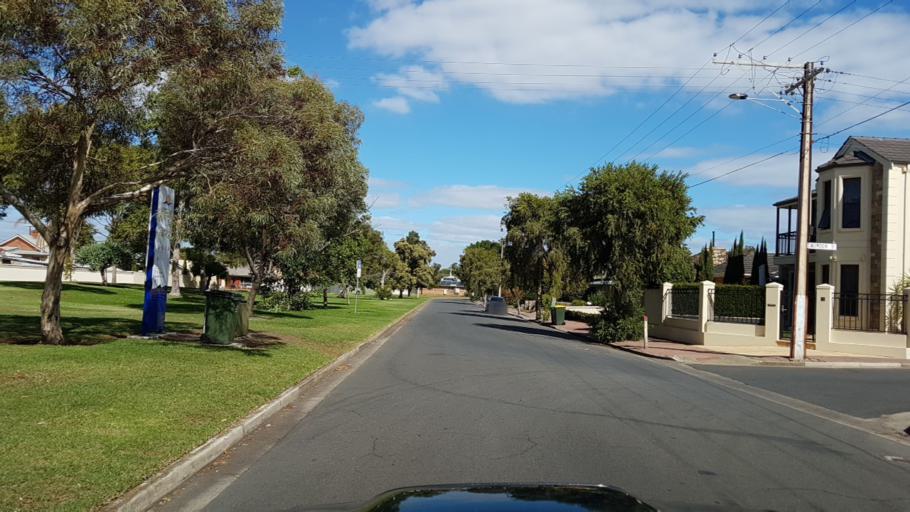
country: AU
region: South Australia
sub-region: Holdfast Bay
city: Glenelg East
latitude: -34.9714
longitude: 138.5242
